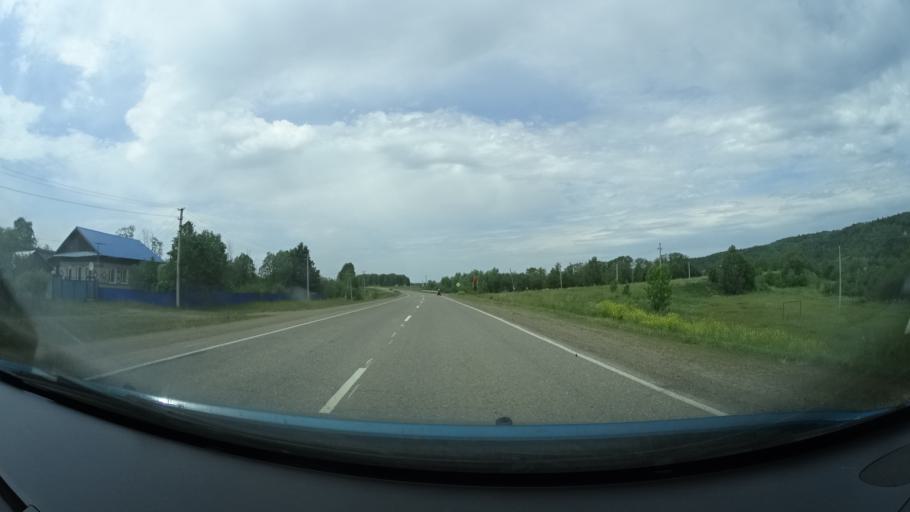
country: RU
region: Perm
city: Barda
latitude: 56.8304
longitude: 55.6246
